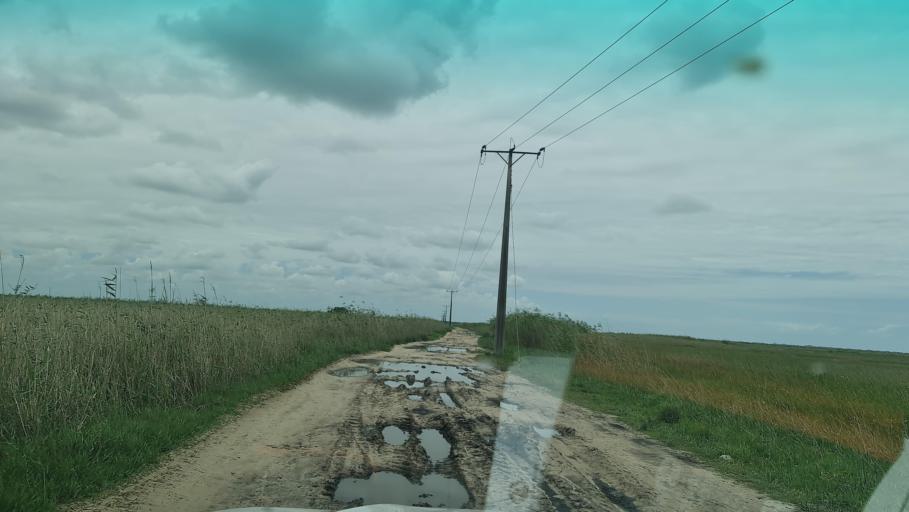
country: MZ
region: Maputo City
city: Maputo
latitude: -25.7210
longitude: 32.6994
